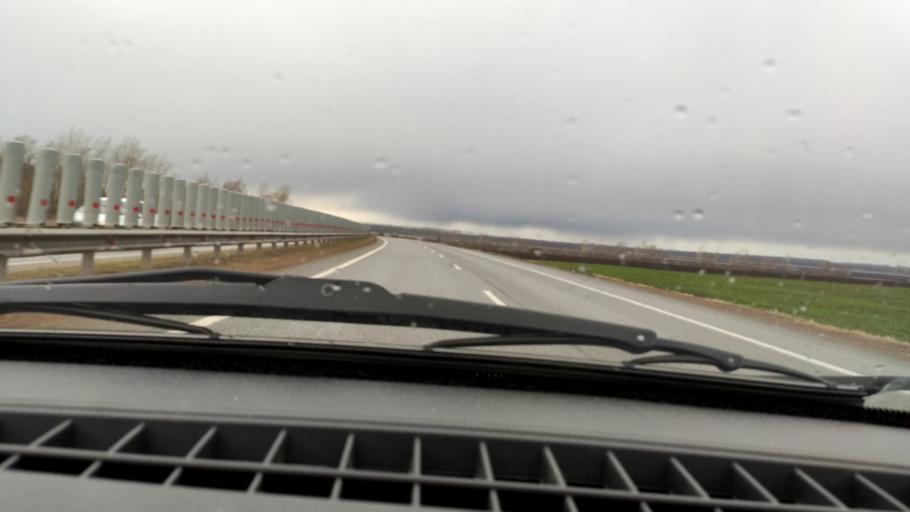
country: RU
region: Bashkortostan
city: Kushnarenkovo
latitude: 55.0649
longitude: 55.3666
